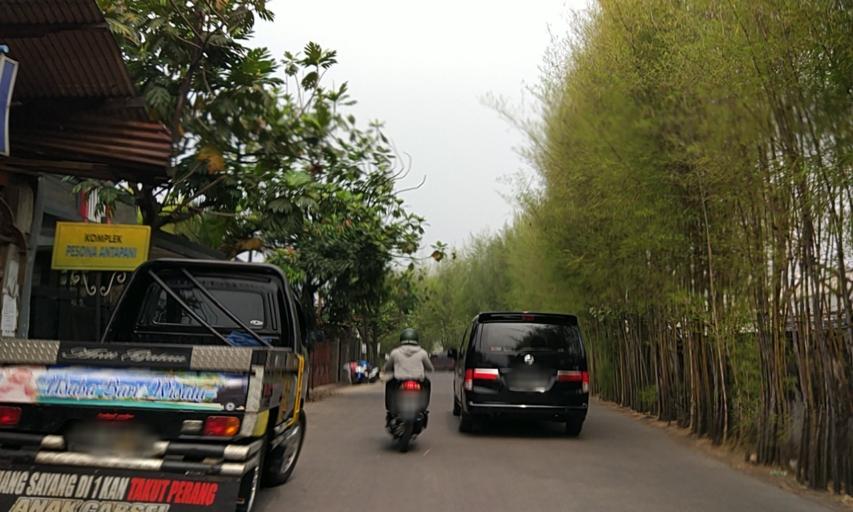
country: ID
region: West Java
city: Bandung
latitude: -6.9052
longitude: 107.6572
